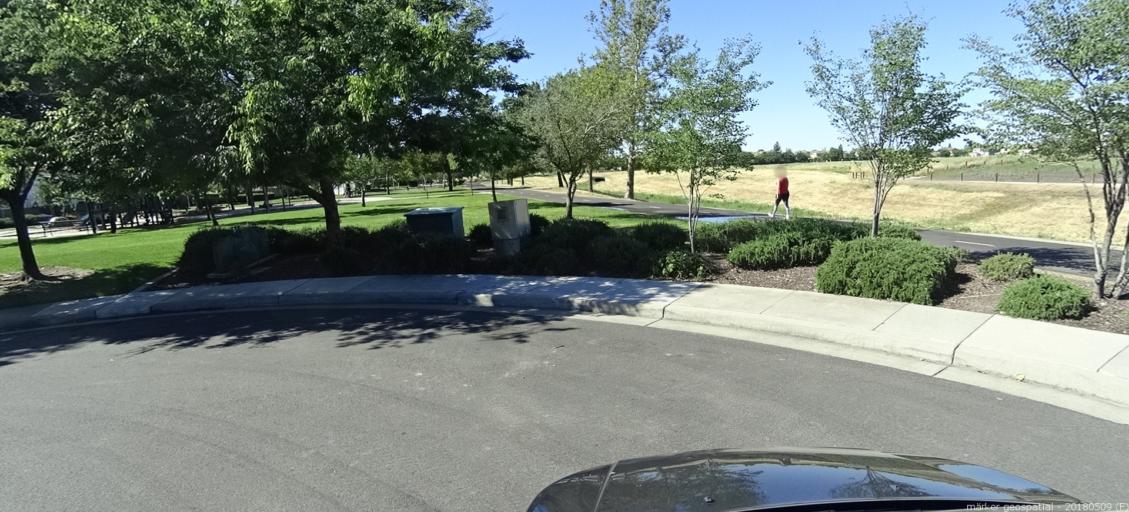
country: US
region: California
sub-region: Sacramento County
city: Elverta
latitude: 38.6688
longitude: -121.5238
